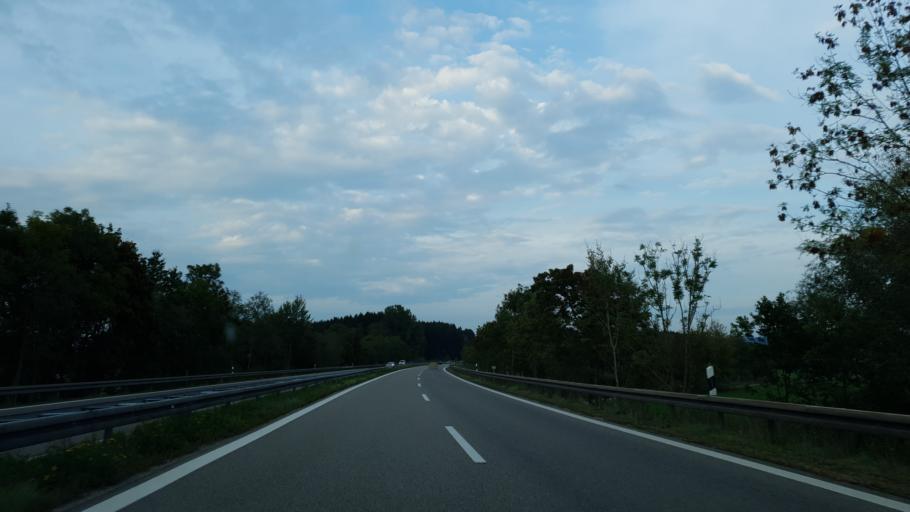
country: DE
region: Bavaria
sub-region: Swabia
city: Waltenhofen
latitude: 47.6764
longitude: 10.2821
